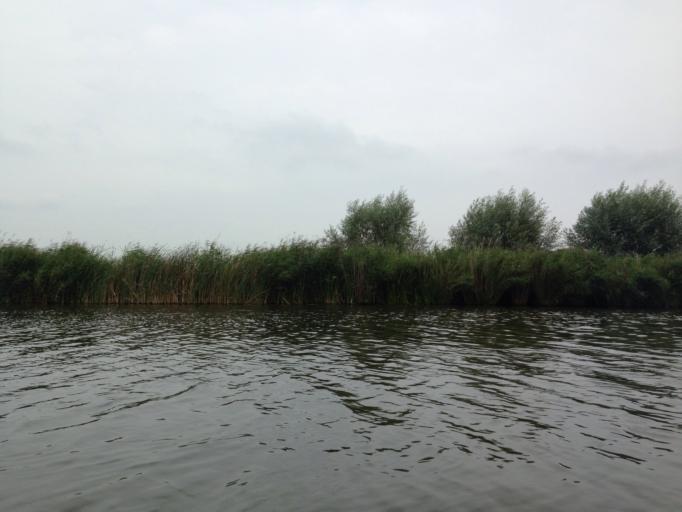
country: NL
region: South Holland
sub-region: Gemeente Vlaardingen
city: Vlaardingen
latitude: 51.9387
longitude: 4.3296
